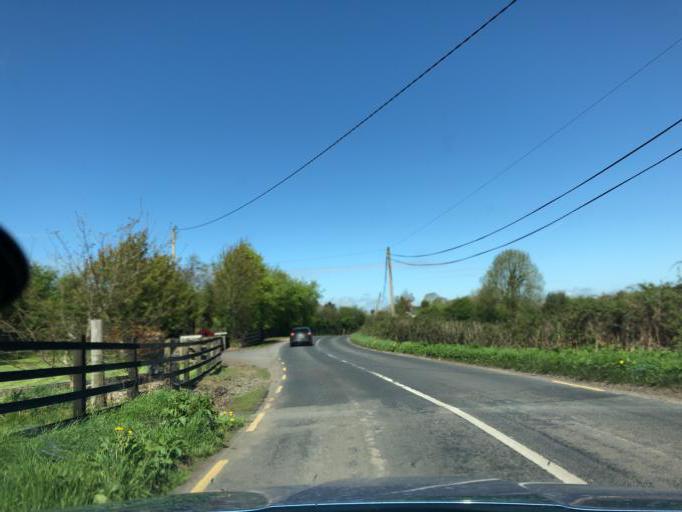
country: IE
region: Connaught
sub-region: County Galway
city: Portumna
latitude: 53.1336
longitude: -8.3573
